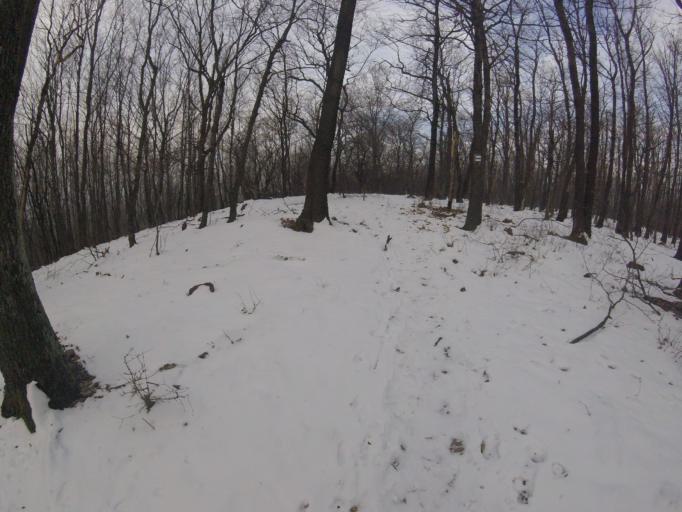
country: HU
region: Heves
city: Recsk
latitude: 47.9005
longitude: 20.1497
